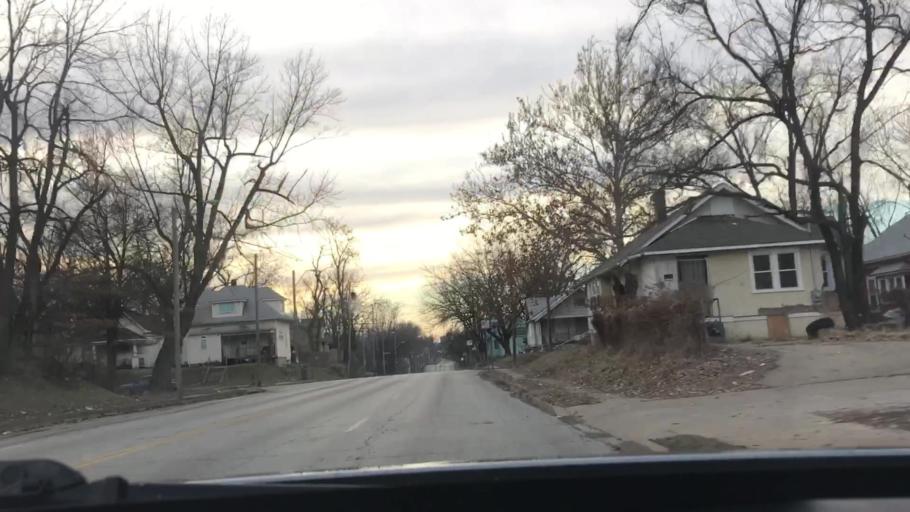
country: US
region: Missouri
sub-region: Jackson County
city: Kansas City
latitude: 39.0835
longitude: -94.5239
